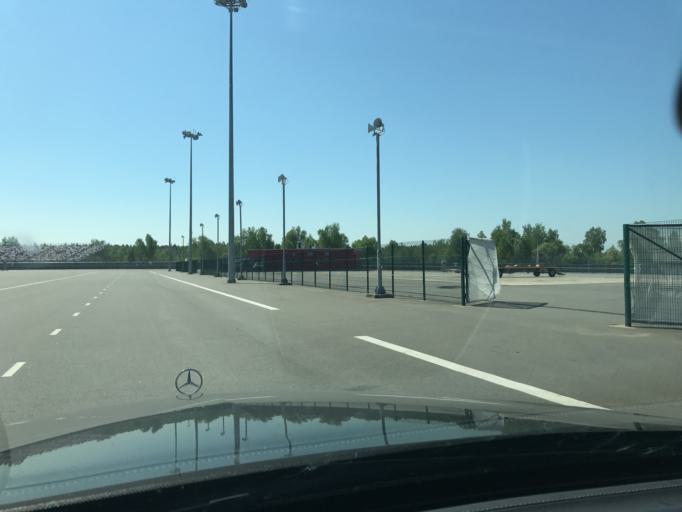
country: RU
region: Moskovskaya
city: Sychevo
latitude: 55.9958
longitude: 36.2685
